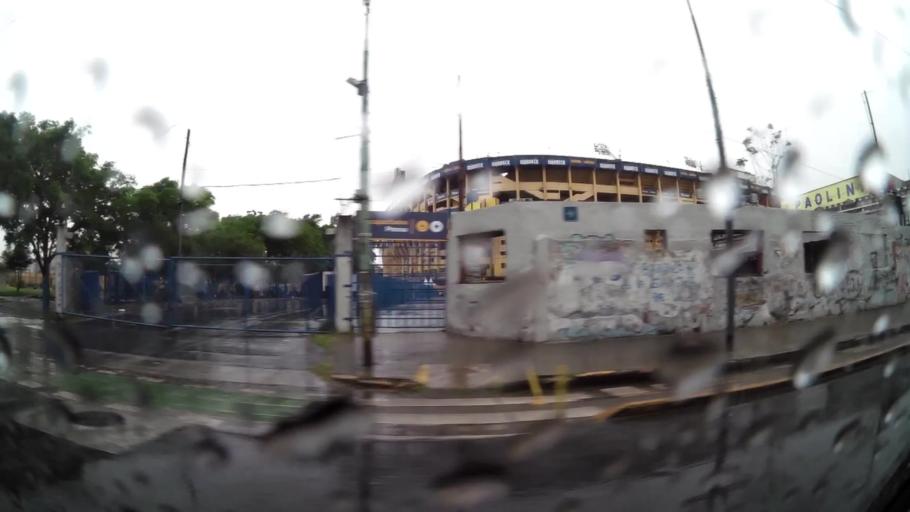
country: AR
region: Buenos Aires F.D.
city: Buenos Aires
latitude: -34.6353
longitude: -58.3669
